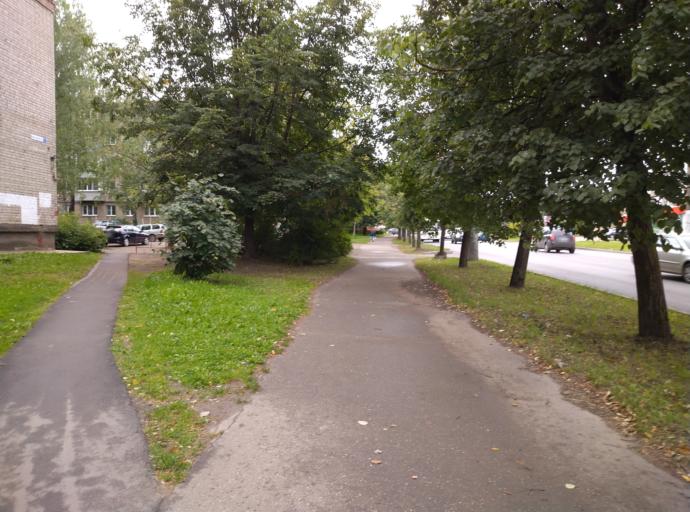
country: RU
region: Kostroma
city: Oktyabr'skiy
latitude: 57.7481
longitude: 40.9697
